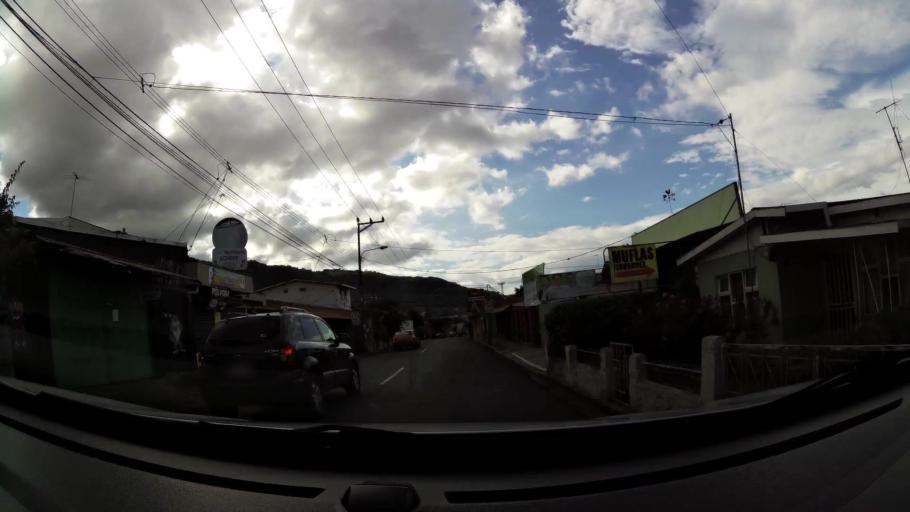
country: CR
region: San Jose
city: Escazu
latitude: 9.9219
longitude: -84.1385
